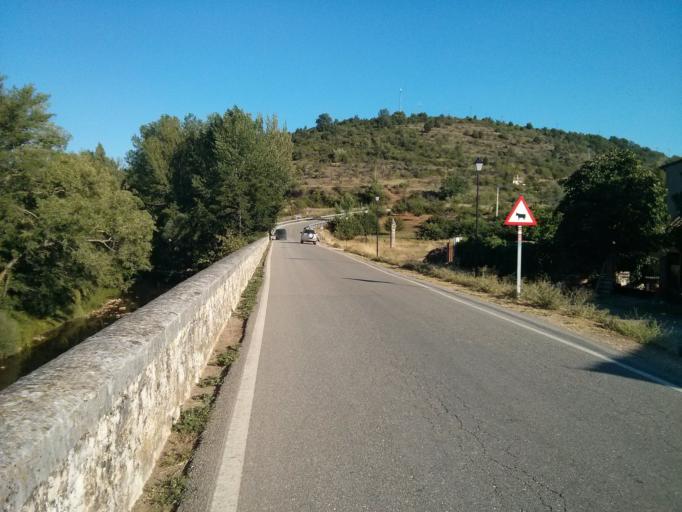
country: ES
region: Castille and Leon
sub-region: Provincia de Burgos
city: Covarrubias
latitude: 42.0570
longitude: -3.5203
